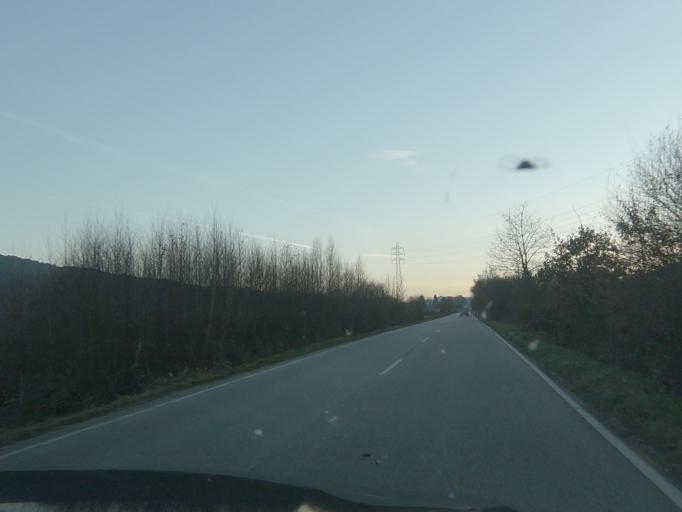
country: PT
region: Vila Real
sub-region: Vila Pouca de Aguiar
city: Vila Pouca de Aguiar
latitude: 41.4569
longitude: -7.6663
